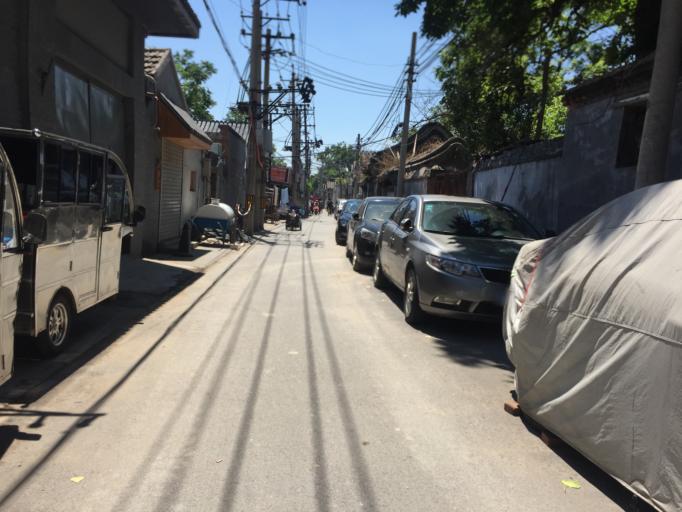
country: CN
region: Beijing
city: Jingshan
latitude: 39.9306
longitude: 116.3875
